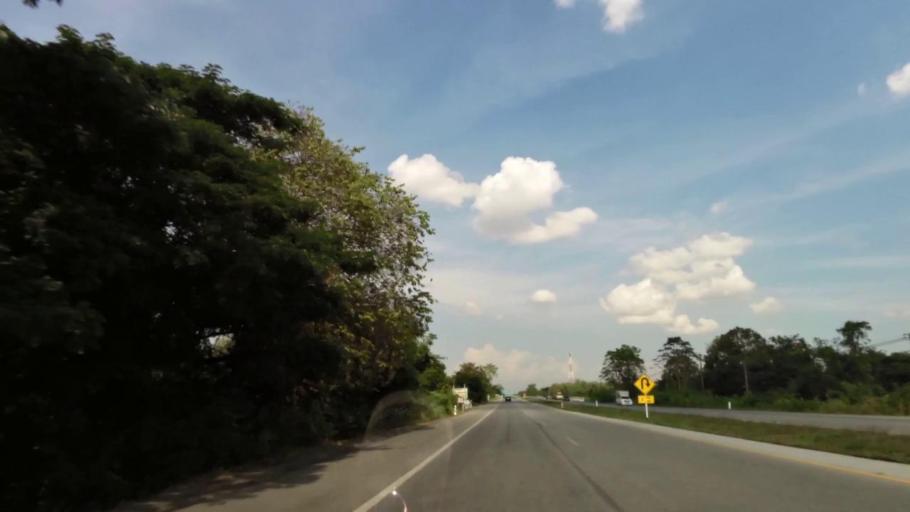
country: TH
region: Uttaradit
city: Thong Saen Khan
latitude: 17.4610
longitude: 100.2376
